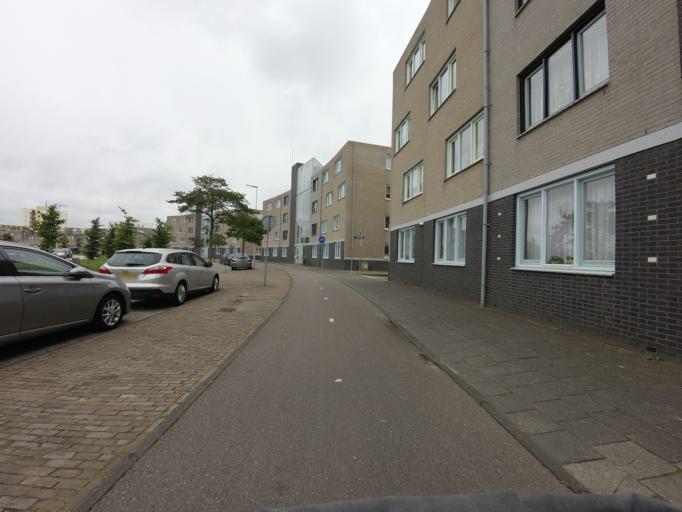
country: NL
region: South Holland
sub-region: Gemeente Voorschoten
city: Voorschoten
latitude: 52.1465
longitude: 4.4511
